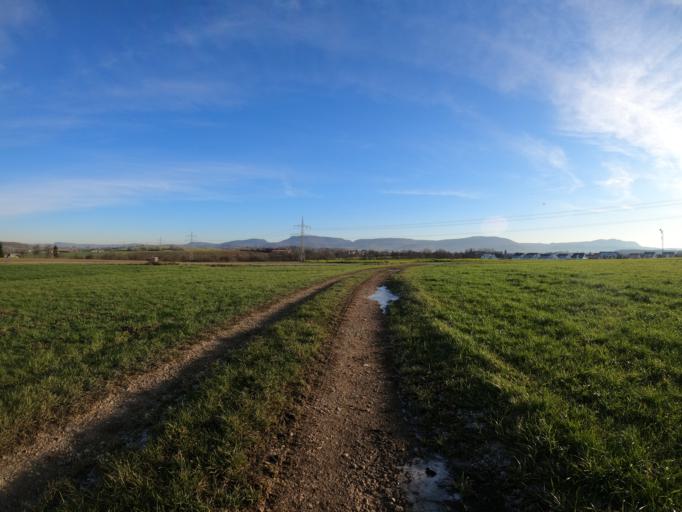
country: DE
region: Baden-Wuerttemberg
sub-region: Regierungsbezirk Stuttgart
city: Boll
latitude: 48.6766
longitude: 9.6096
